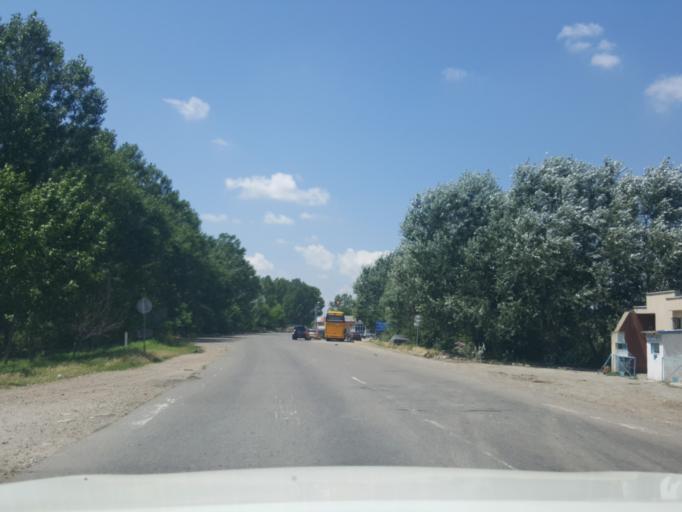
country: UA
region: Odessa
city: Bilyayivka
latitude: 46.4120
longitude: 30.1243
